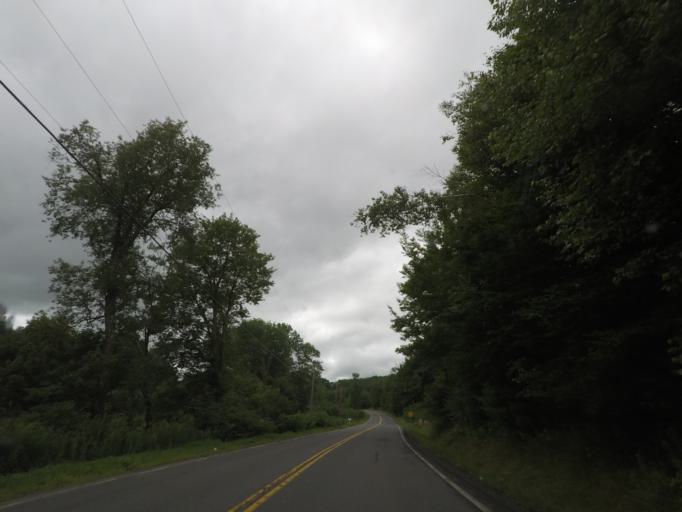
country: US
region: New York
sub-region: Rensselaer County
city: Poestenkill
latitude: 42.6867
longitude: -73.4904
